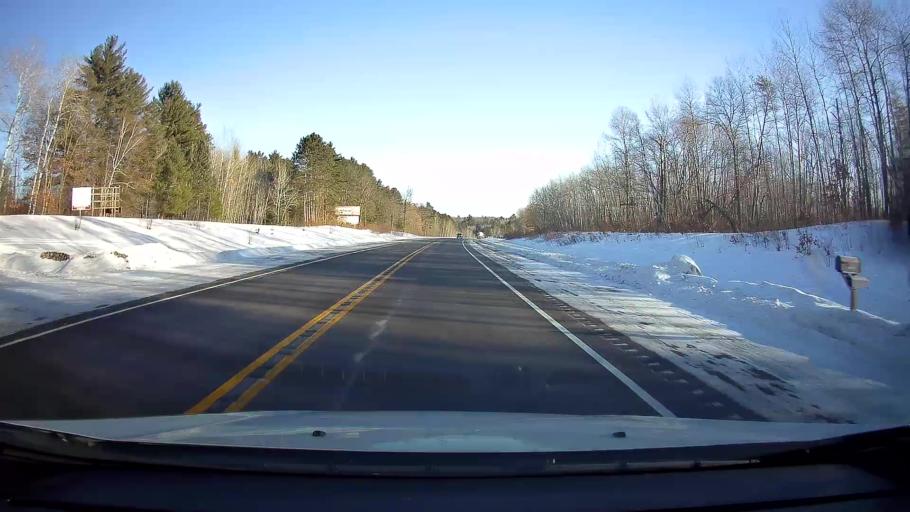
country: US
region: Wisconsin
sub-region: Sawyer County
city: Hayward
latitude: 46.0660
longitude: -91.4362
